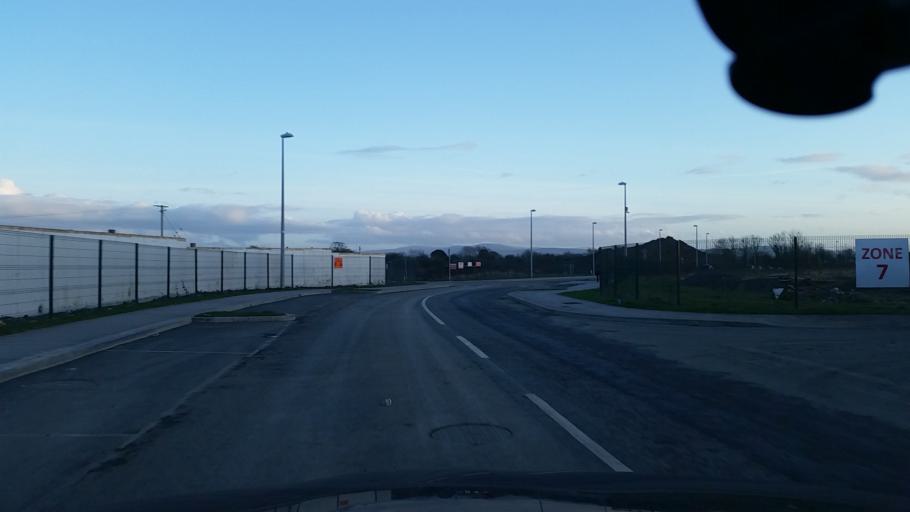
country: IE
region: Leinster
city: Hartstown
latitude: 53.3899
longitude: -6.4400
